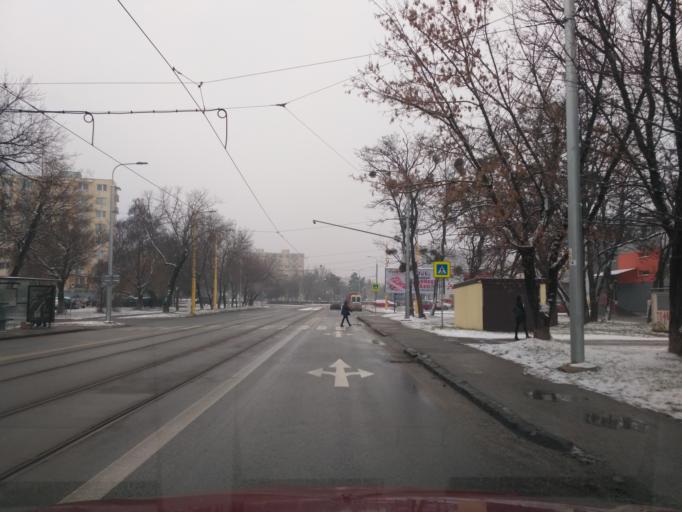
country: SK
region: Kosicky
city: Kosice
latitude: 48.7059
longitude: 21.2381
